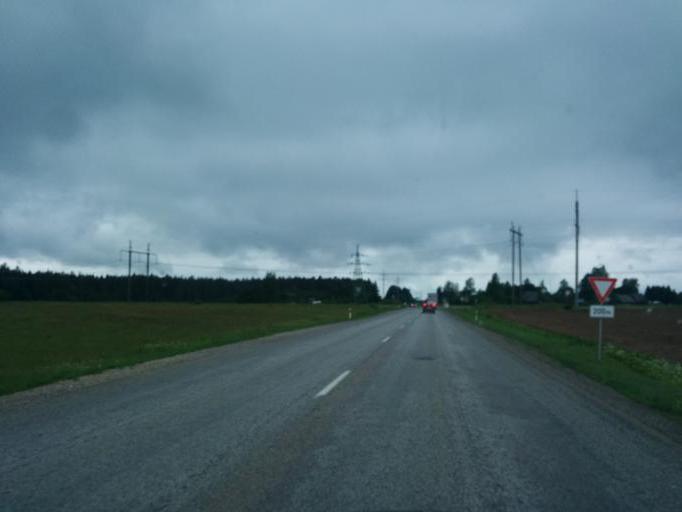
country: LV
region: Beverina
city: Murmuiza
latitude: 57.5091
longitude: 25.4540
